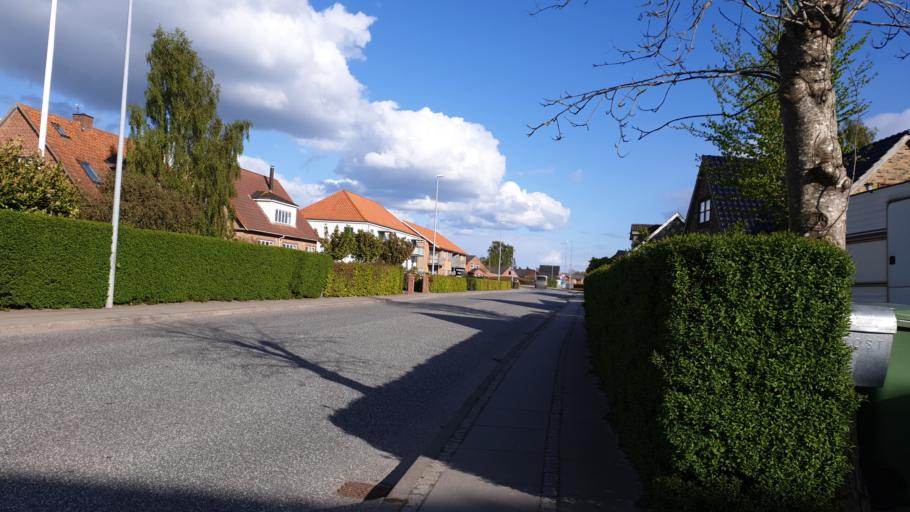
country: DK
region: Central Jutland
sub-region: Hedensted Kommune
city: Hedensted
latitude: 55.8045
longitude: 9.6902
